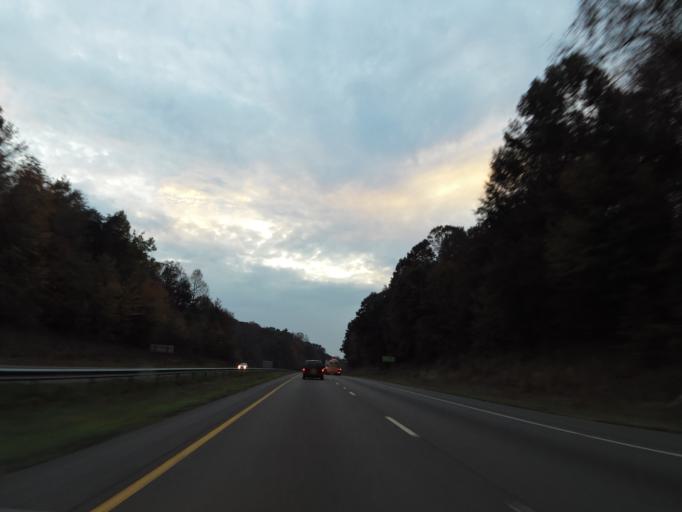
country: US
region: North Carolina
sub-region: Burke County
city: Salem
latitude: 35.7181
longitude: -81.7058
